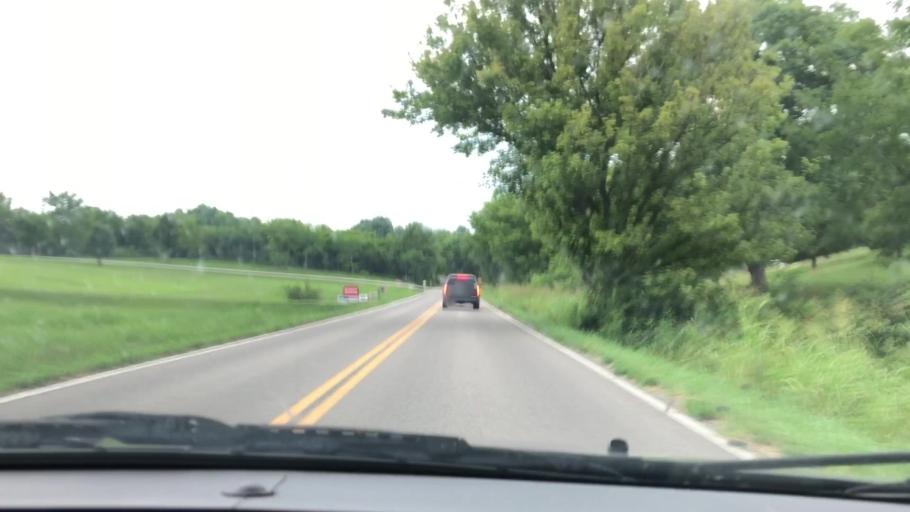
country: US
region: Tennessee
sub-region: Maury County
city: Spring Hill
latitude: 35.7204
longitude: -87.0129
